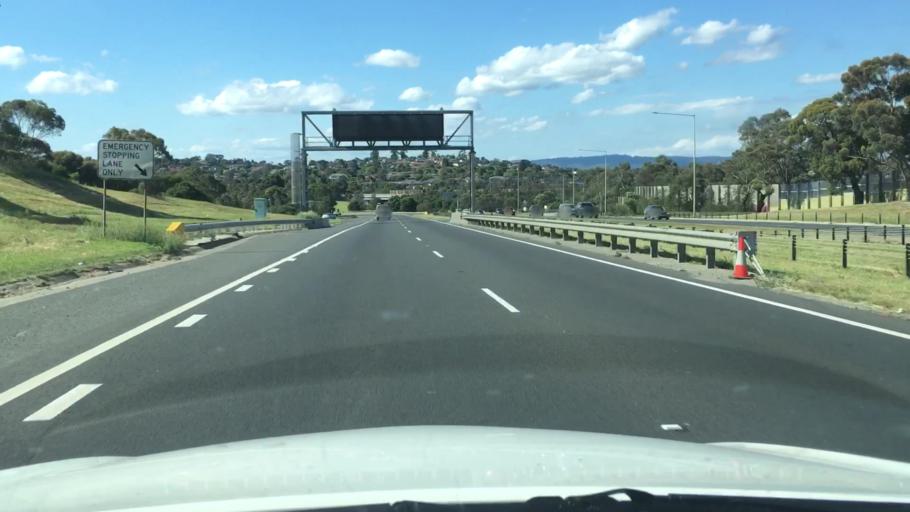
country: AU
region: Victoria
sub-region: Casey
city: Eumemmerring
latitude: -37.9962
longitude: 145.2530
